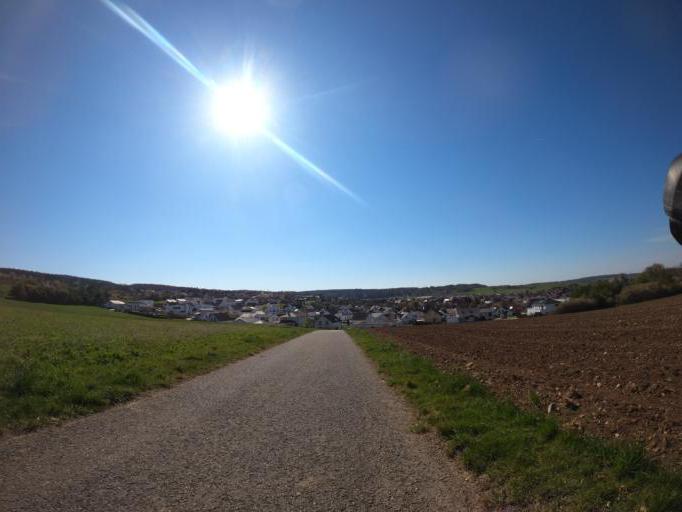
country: DE
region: Baden-Wuerttemberg
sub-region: Karlsruhe Region
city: Wiernsheim
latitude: 48.8887
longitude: 8.8620
